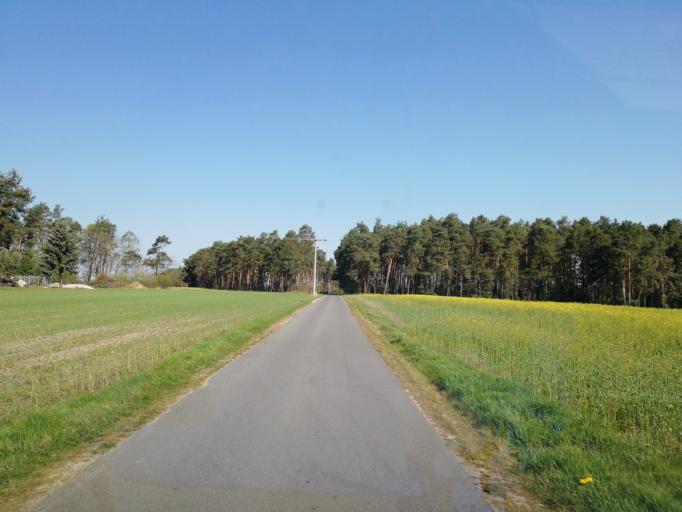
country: DE
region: Brandenburg
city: Sallgast
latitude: 51.6498
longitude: 13.8572
